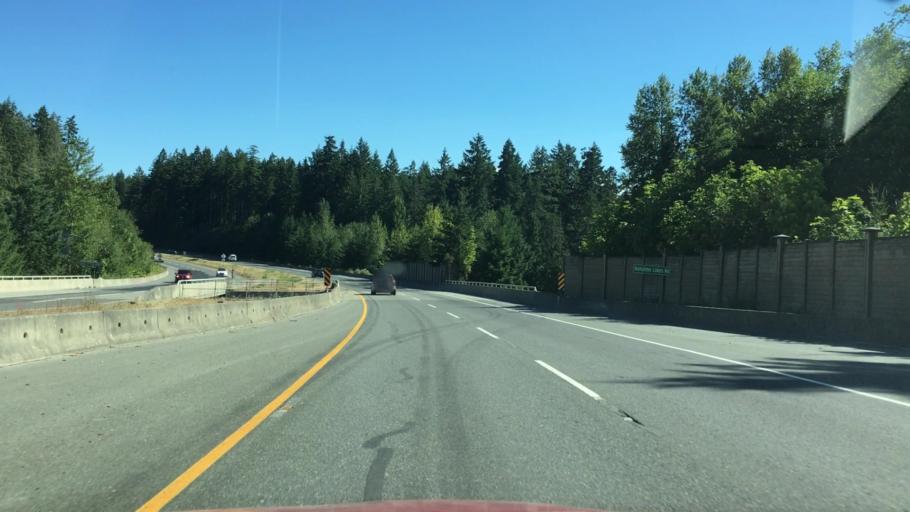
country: CA
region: British Columbia
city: Nanaimo
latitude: 49.1471
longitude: -123.9727
